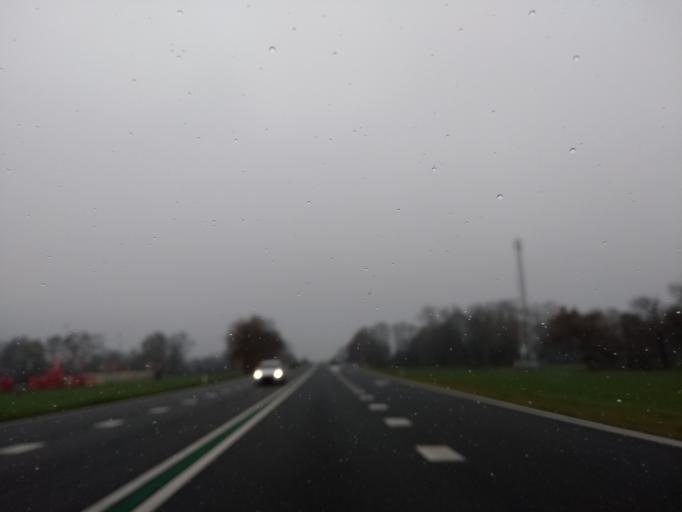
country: NL
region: Overijssel
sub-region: Gemeente Twenterand
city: Vriezenveen
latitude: 52.4119
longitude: 6.6357
